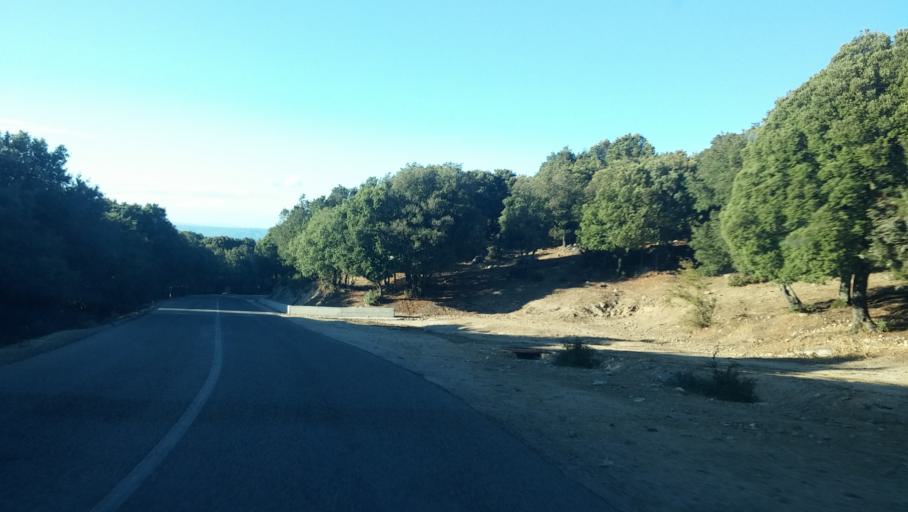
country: IT
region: Sardinia
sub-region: Provincia di Nuoro
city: Orgosolo
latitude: 40.1907
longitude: 9.3532
